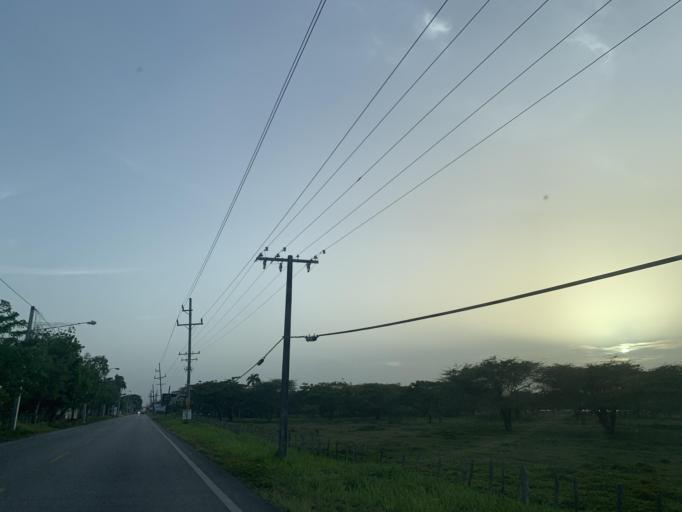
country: DO
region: Puerto Plata
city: Cabarete
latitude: 19.7762
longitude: -70.4890
